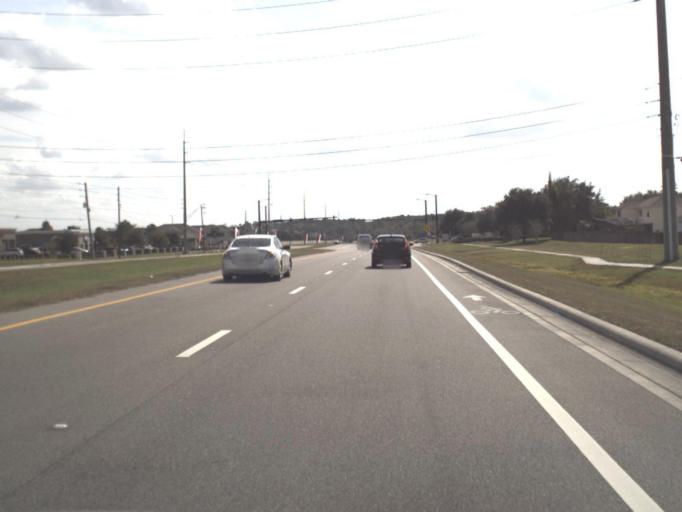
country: US
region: Florida
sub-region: Osceola County
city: Campbell
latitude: 28.2272
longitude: -81.4861
